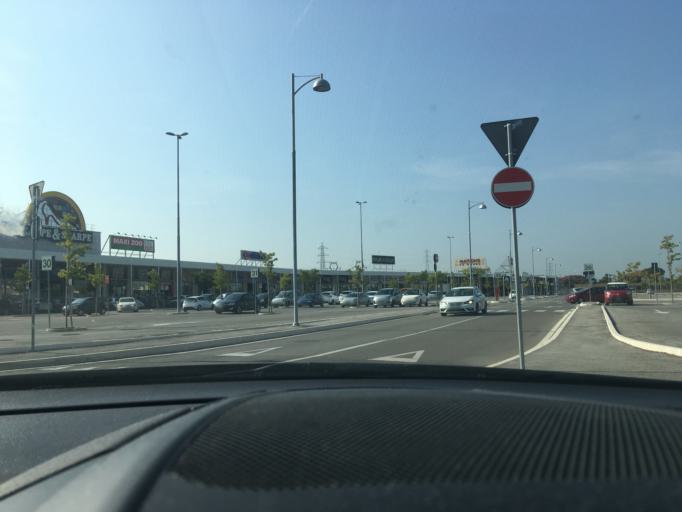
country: IT
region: Emilia-Romagna
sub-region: Forli-Cesena
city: Gatteo a Mare
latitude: 44.1575
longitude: 12.4308
